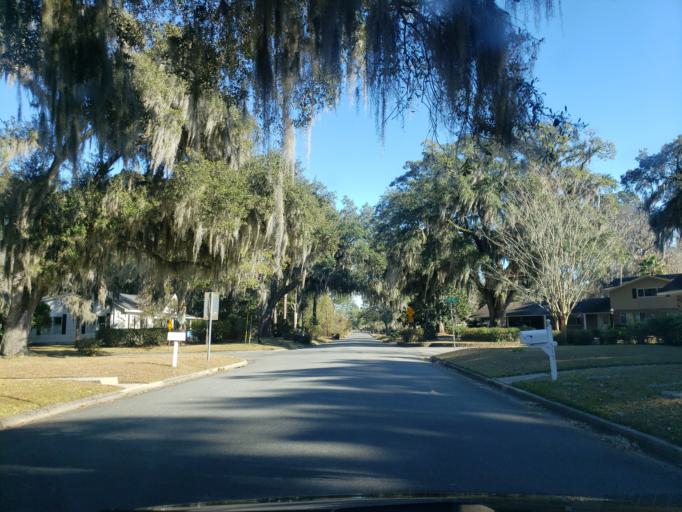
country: US
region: Georgia
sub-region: Chatham County
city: Thunderbolt
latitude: 32.0194
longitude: -81.1005
